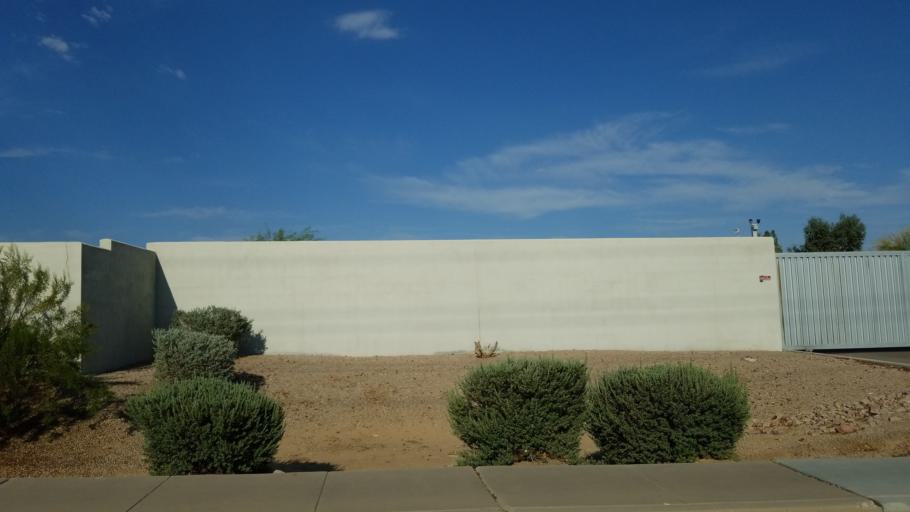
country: US
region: Arizona
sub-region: Maricopa County
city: Tempe
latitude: 33.4480
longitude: -111.9179
